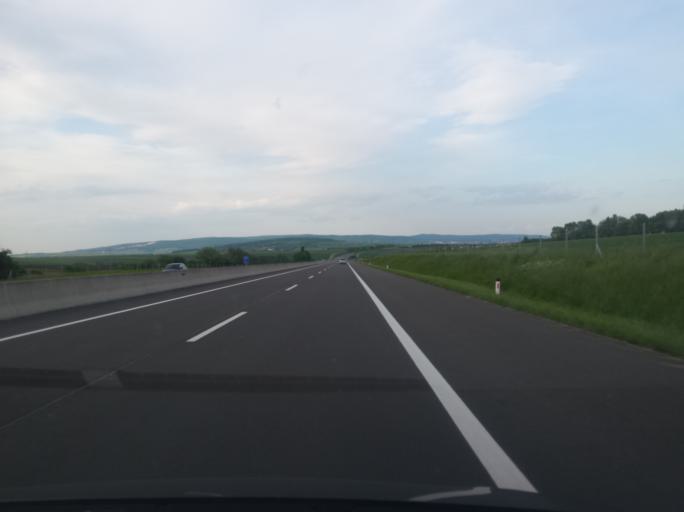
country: AT
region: Burgenland
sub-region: Politischer Bezirk Mattersburg
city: Hirm
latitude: 47.7787
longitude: 16.4350
